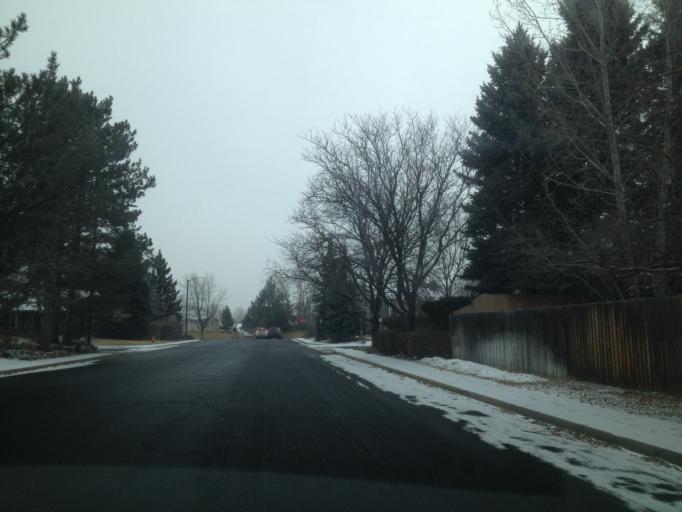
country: US
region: Colorado
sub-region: Boulder County
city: Superior
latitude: 39.9663
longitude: -105.1528
